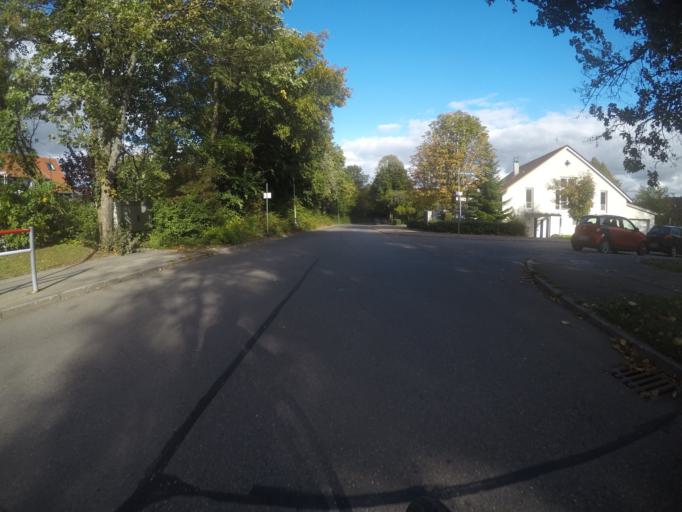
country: DE
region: Baden-Wuerttemberg
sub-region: Regierungsbezirk Stuttgart
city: Gerlingen
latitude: 48.7496
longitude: 9.0808
